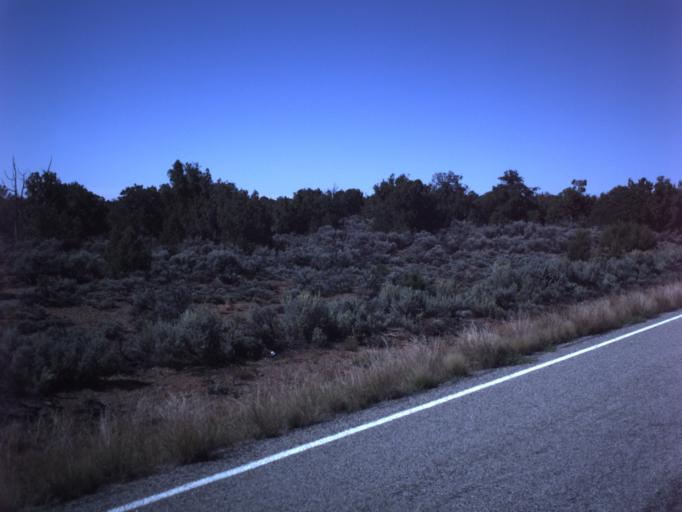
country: US
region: Utah
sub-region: San Juan County
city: Blanding
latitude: 37.3310
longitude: -109.9136
